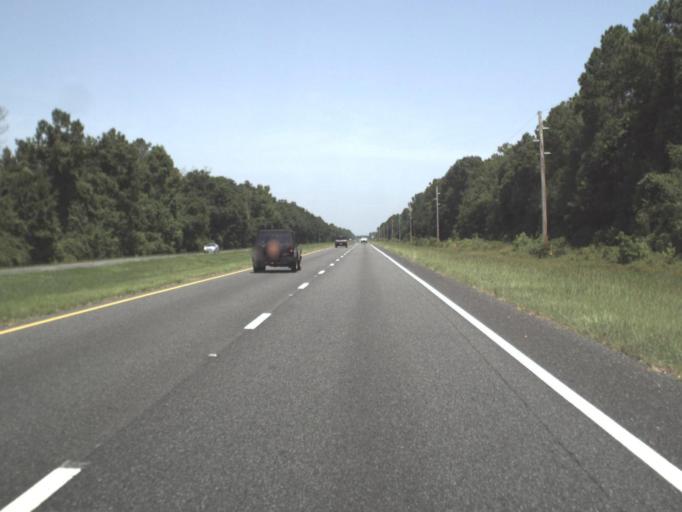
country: US
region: Florida
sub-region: Taylor County
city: Steinhatchee
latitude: 29.6956
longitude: -83.2781
